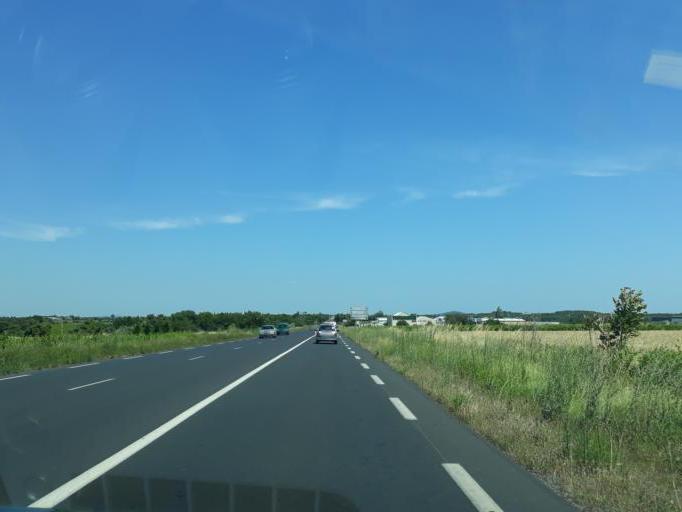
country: FR
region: Languedoc-Roussillon
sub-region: Departement de l'Herault
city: Portiragnes
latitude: 43.3132
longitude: 3.3335
